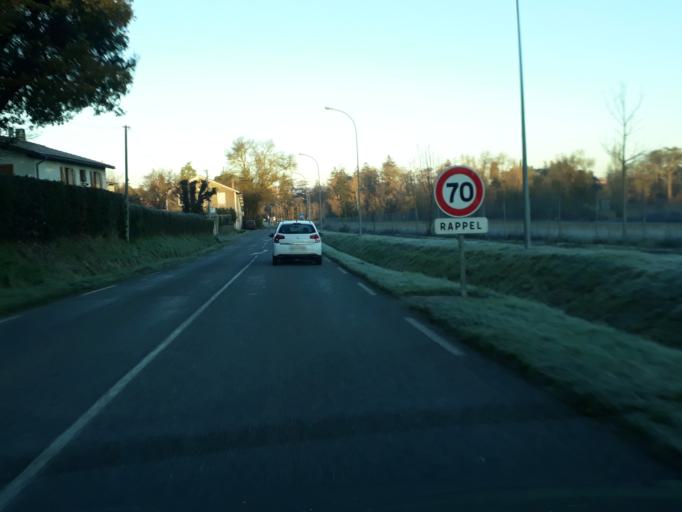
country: FR
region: Midi-Pyrenees
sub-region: Departement du Gers
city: Auch
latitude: 43.6366
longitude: 0.6048
